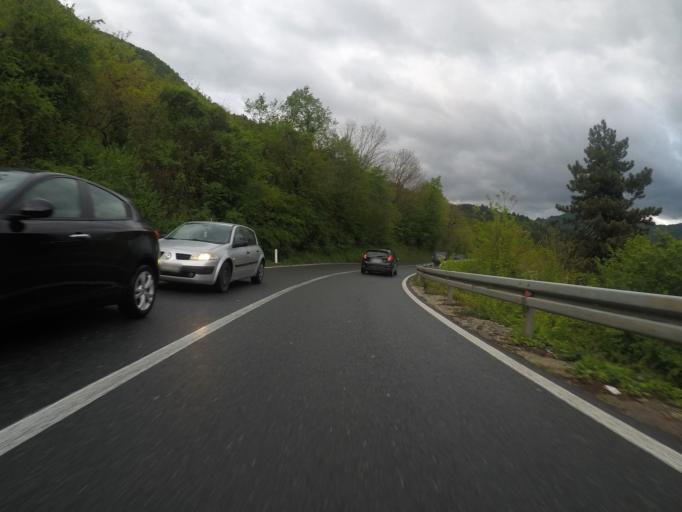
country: BA
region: Federation of Bosnia and Herzegovina
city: Jablanica
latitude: 43.6475
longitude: 17.7558
